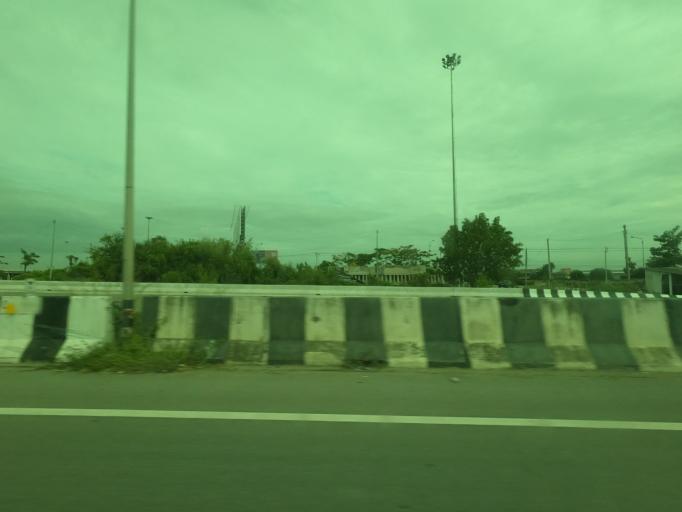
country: TH
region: Nonthaburi
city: Bang Bua Thong
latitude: 13.9408
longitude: 100.4214
